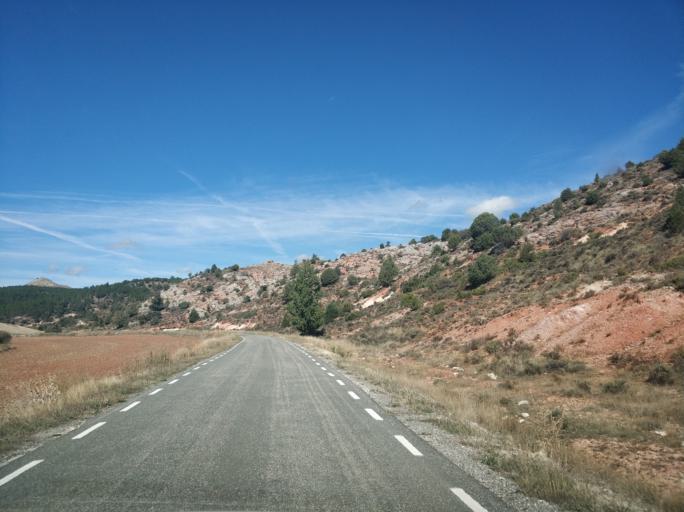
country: ES
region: Castille and Leon
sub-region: Provincia de Soria
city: Espeja de San Marcelino
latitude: 41.8111
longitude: -3.2241
